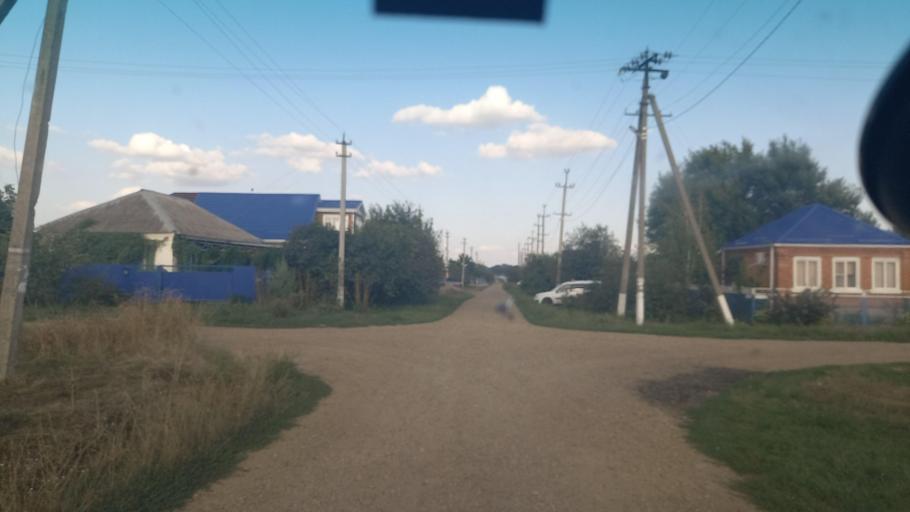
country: RU
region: Adygeya
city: Khatukay
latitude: 45.2973
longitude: 39.5684
